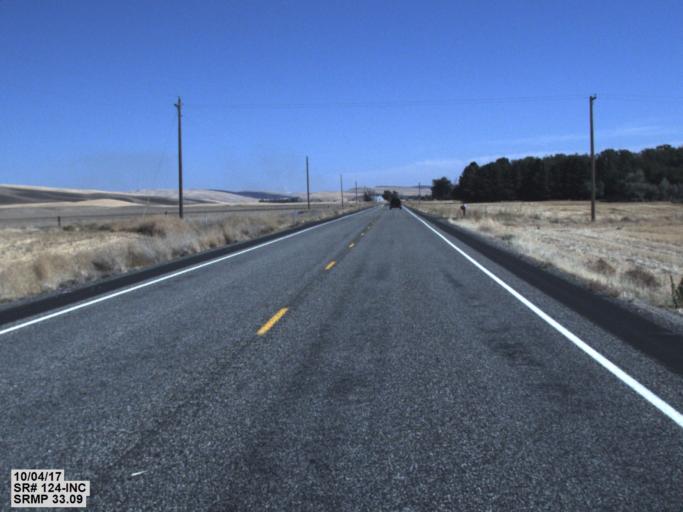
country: US
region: Washington
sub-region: Walla Walla County
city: Waitsburg
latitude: 46.2995
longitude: -118.3783
